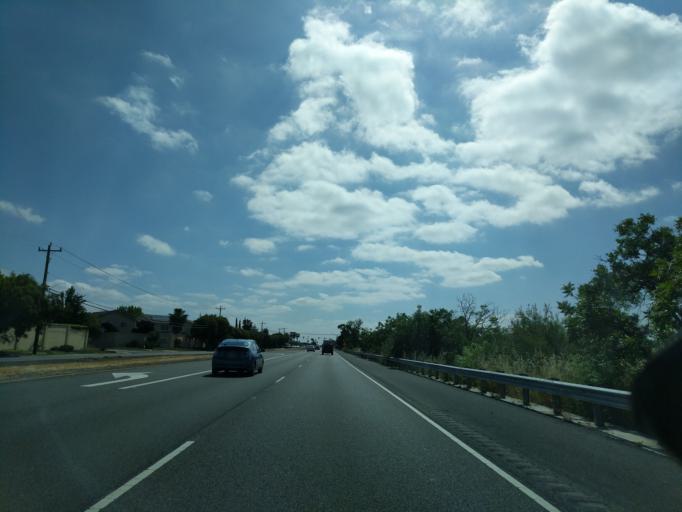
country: US
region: California
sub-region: Contra Costa County
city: Byron
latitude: 37.8893
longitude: -121.6247
